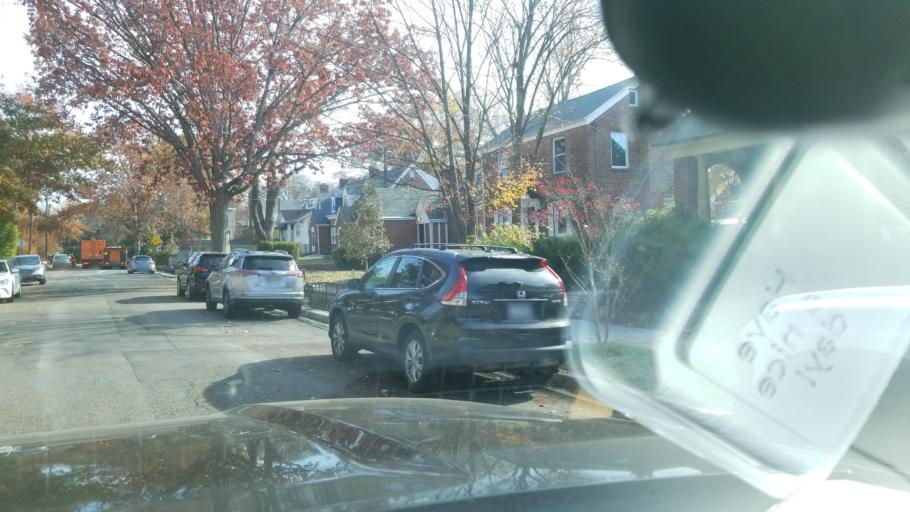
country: US
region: Maryland
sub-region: Prince George's County
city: Chillum
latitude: 38.9577
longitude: -77.0080
